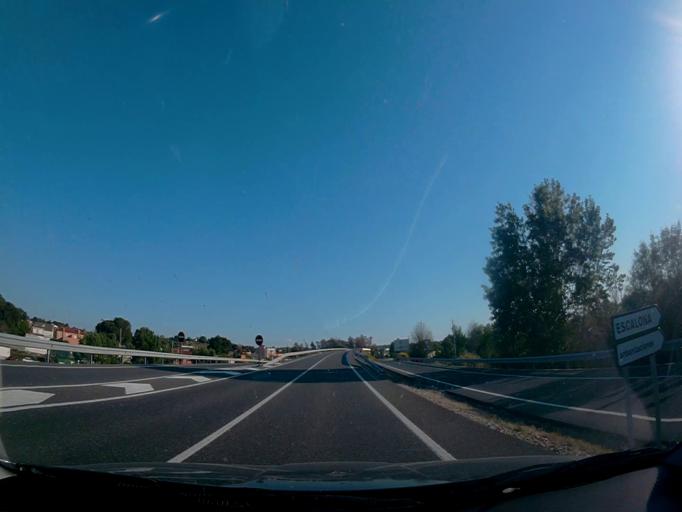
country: ES
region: Castille-La Mancha
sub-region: Province of Toledo
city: Escalona
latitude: 40.1616
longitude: -4.3982
